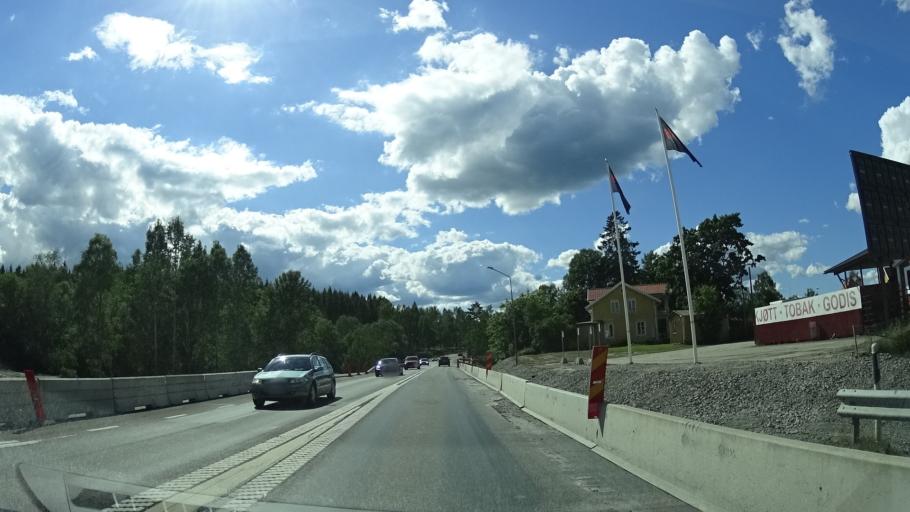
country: SE
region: Vaermland
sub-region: Arjangs Kommun
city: Toecksfors
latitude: 59.5075
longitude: 11.8408
